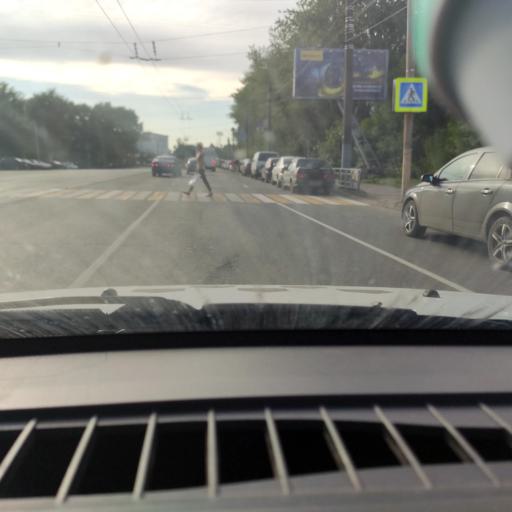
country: RU
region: Kirov
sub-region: Kirovo-Chepetskiy Rayon
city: Kirov
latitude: 58.6196
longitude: 49.6590
